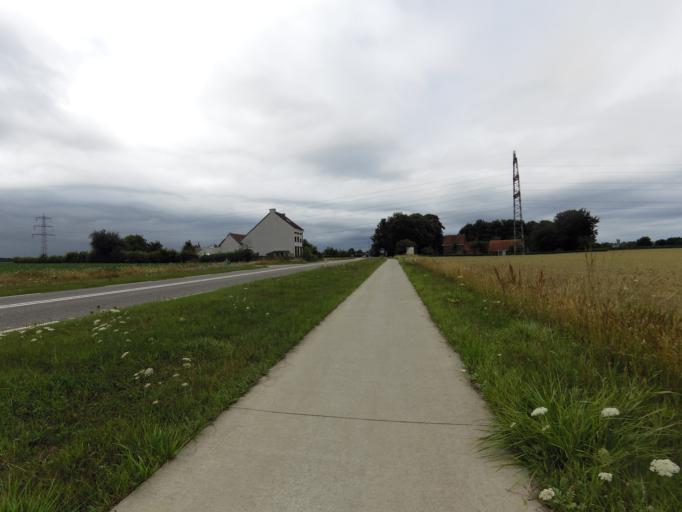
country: NL
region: Limburg
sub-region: Gemeente Nuth
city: Nuth
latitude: 50.9037
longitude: 5.8576
